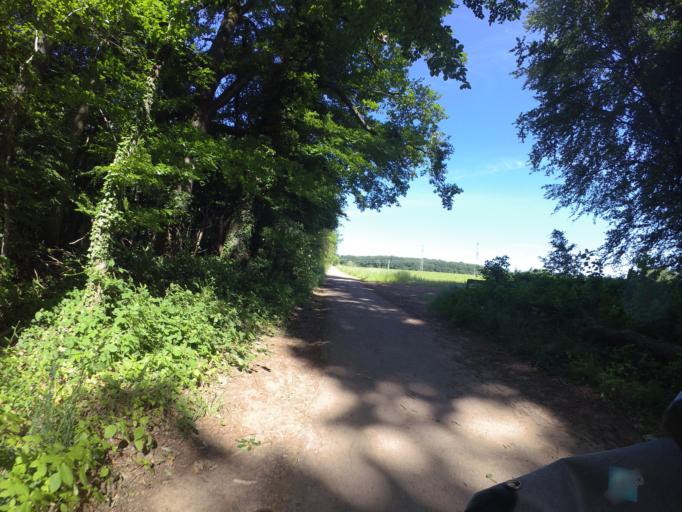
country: DE
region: Rheinland-Pfalz
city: Dunzweiler
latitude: 49.3781
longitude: 7.2924
